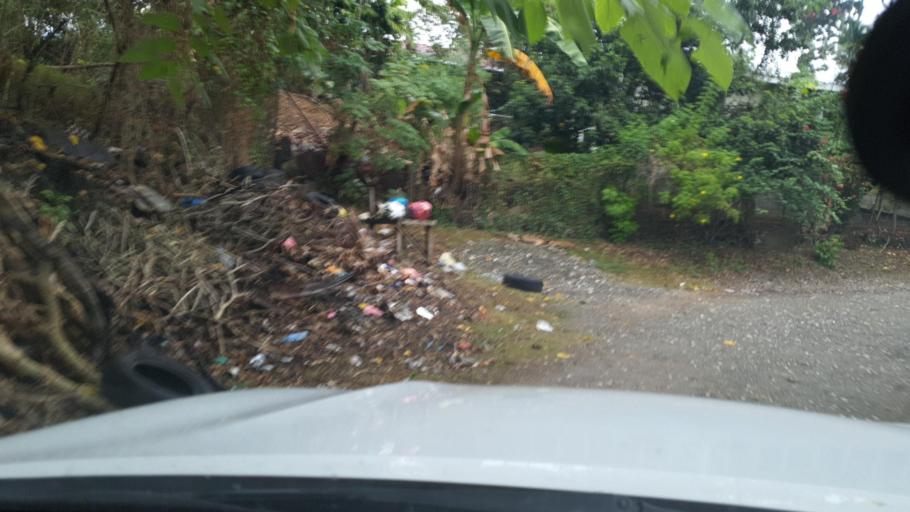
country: SB
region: Guadalcanal
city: Honiara
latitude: -9.4415
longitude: 159.9791
